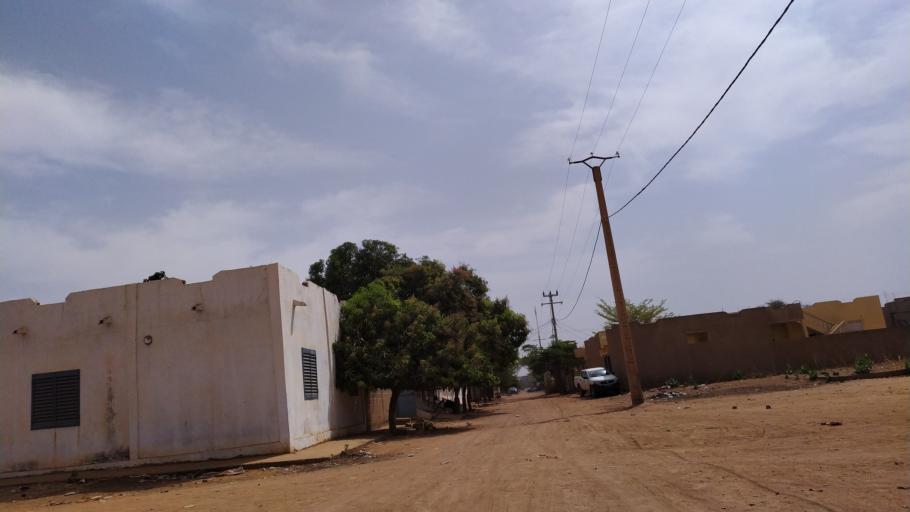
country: ML
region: Kayes
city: Kayes
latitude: 14.4547
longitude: -11.4651
